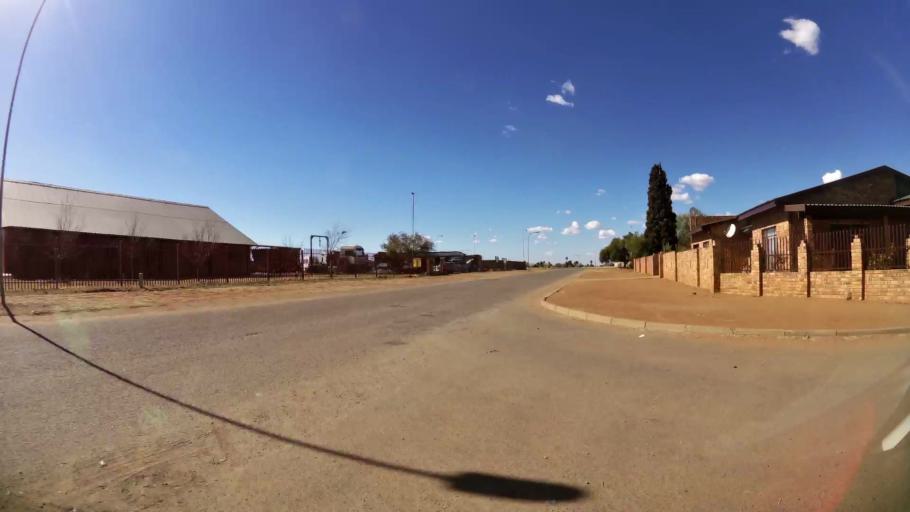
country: ZA
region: North-West
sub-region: Dr Kenneth Kaunda District Municipality
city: Klerksdorp
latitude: -26.8686
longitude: 26.5871
